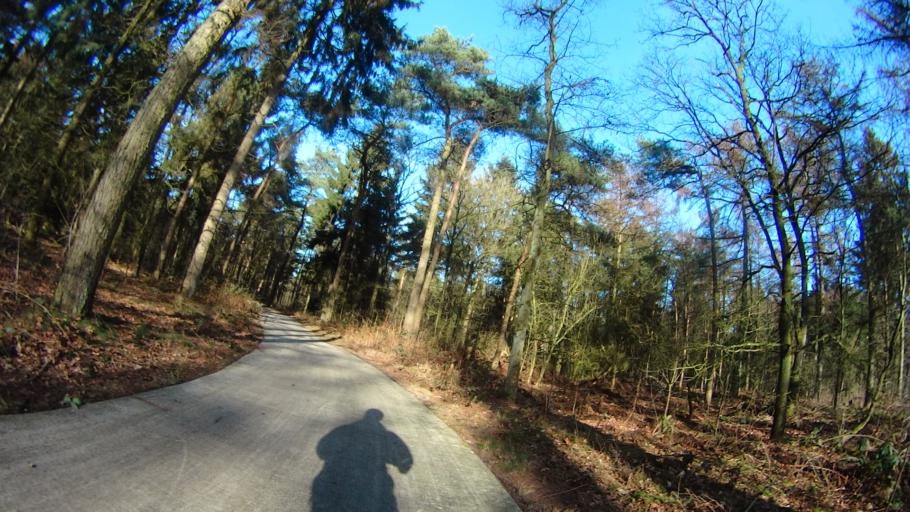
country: NL
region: Drenthe
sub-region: Gemeente Coevorden
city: Sleen
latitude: 52.7617
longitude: 6.8553
